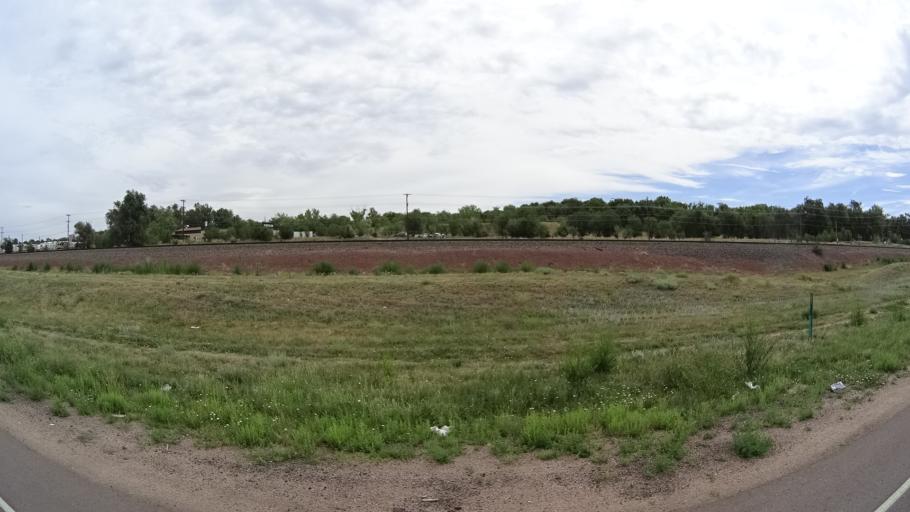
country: US
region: Colorado
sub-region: El Paso County
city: Fountain
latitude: 38.6991
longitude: -104.7070
